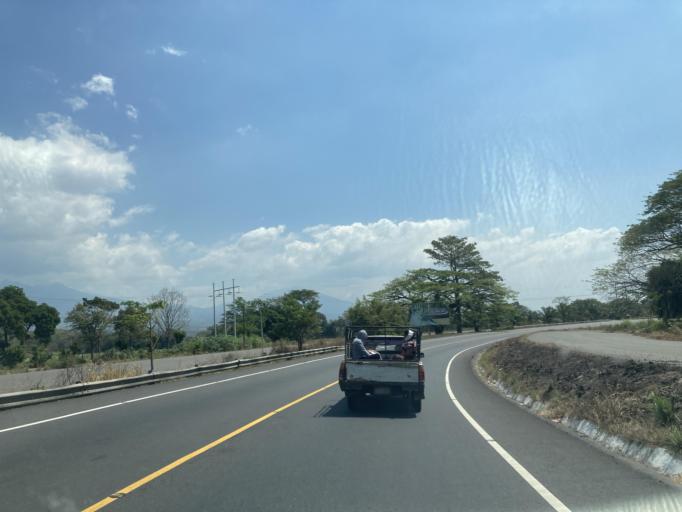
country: GT
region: Escuintla
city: Guanagazapa
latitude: 14.1157
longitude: -90.6376
